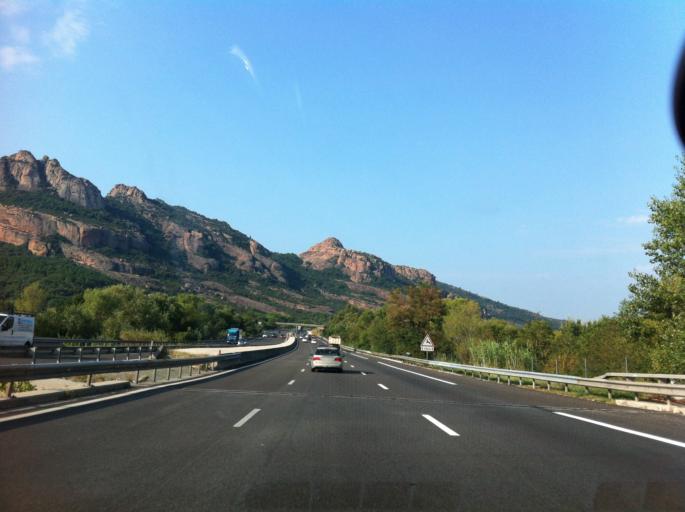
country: FR
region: Provence-Alpes-Cote d'Azur
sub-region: Departement du Var
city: Roquebrune-sur-Argens
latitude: 43.4624
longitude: 6.6160
